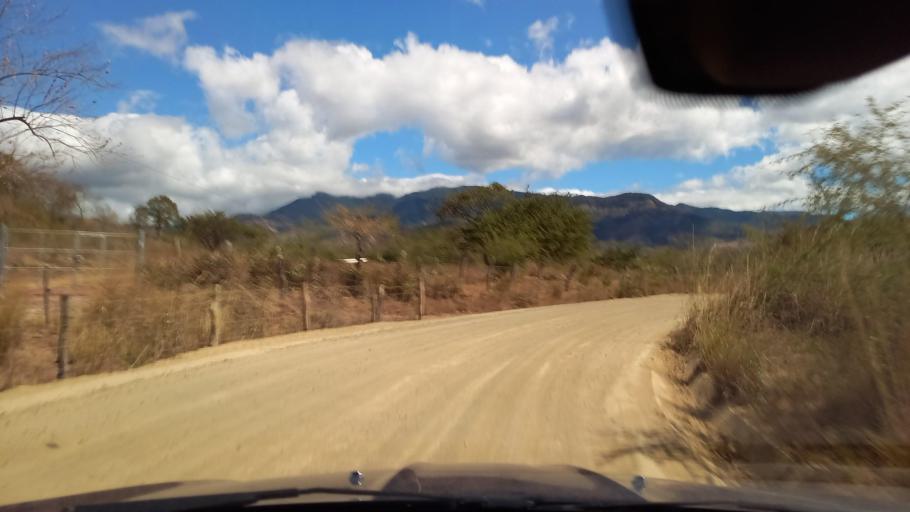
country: SV
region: Santa Ana
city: Metapan
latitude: 14.3608
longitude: -89.4635
